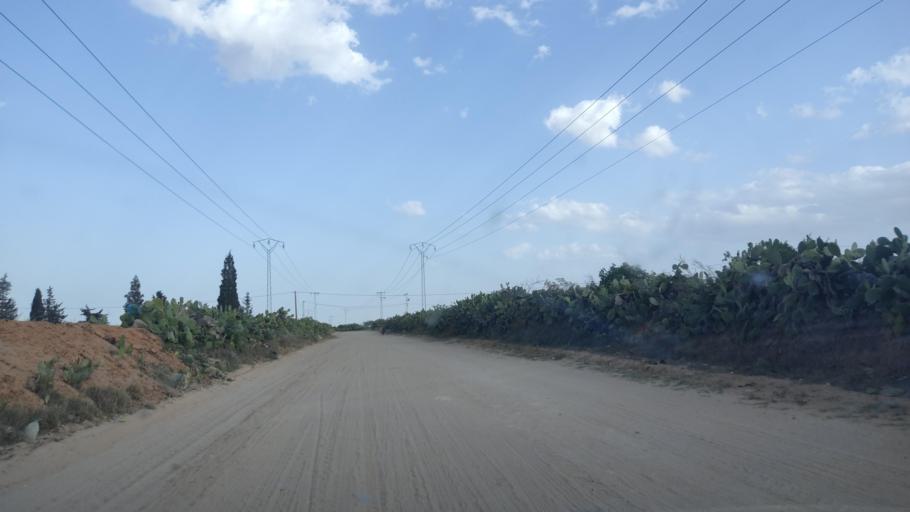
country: TN
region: Safaqis
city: Sfax
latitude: 34.8573
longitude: 10.6041
